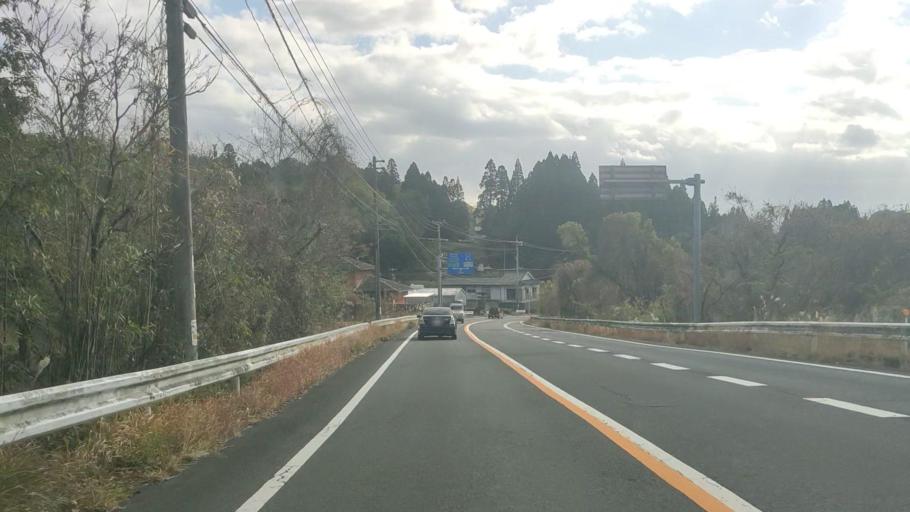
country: JP
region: Kagoshima
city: Kajiki
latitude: 31.7591
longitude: 130.6785
